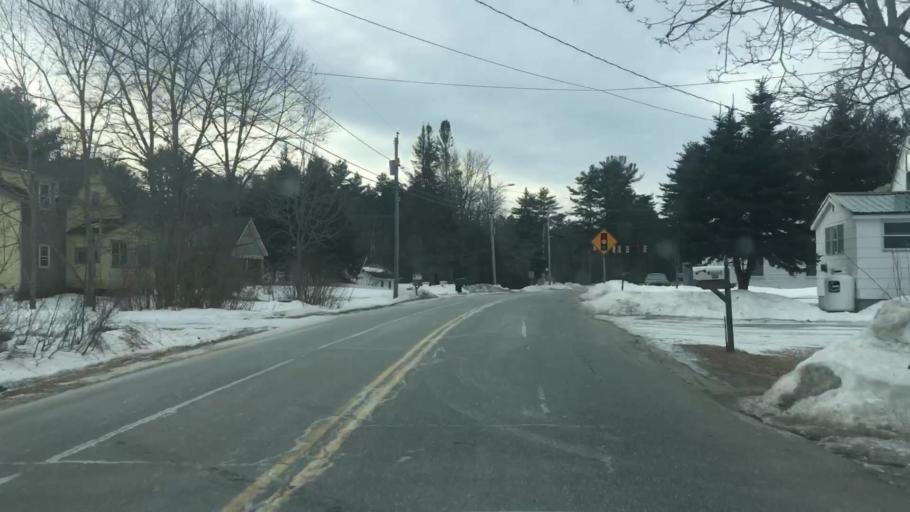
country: US
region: Maine
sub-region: Kennebec County
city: Chelsea
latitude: 44.2882
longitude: -69.6997
